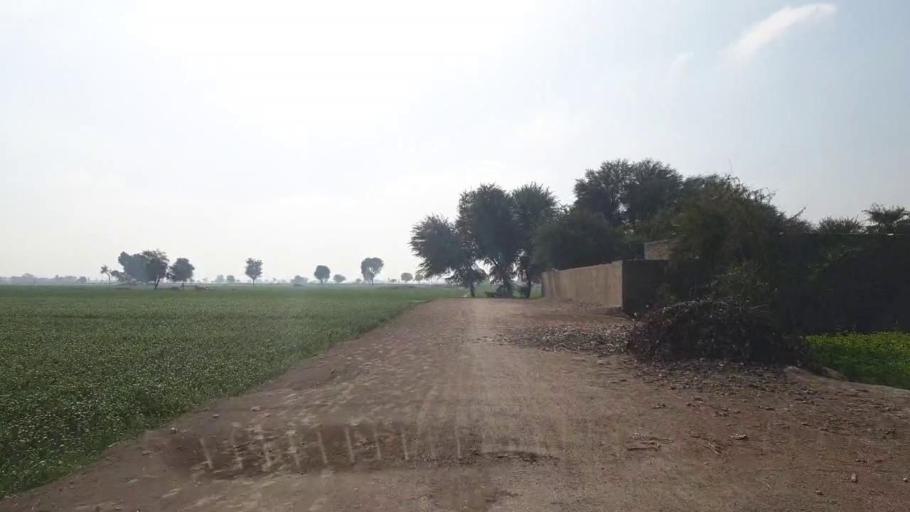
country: PK
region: Sindh
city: Shahdadpur
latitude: 26.0200
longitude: 68.5744
